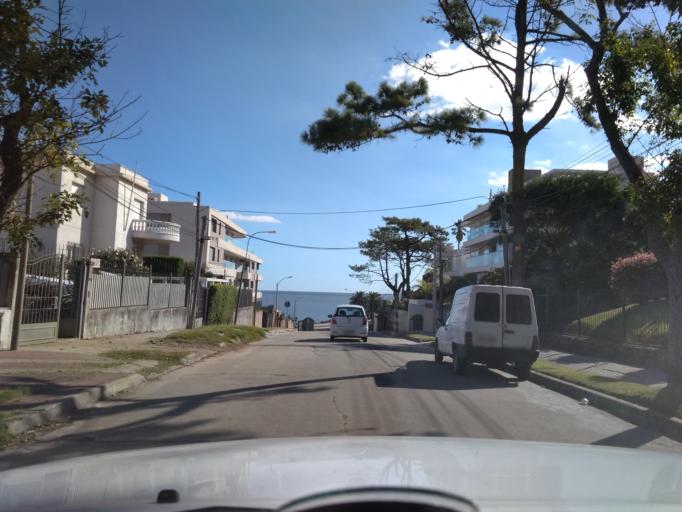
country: UY
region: Canelones
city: Paso de Carrasco
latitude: -34.8942
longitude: -56.0839
